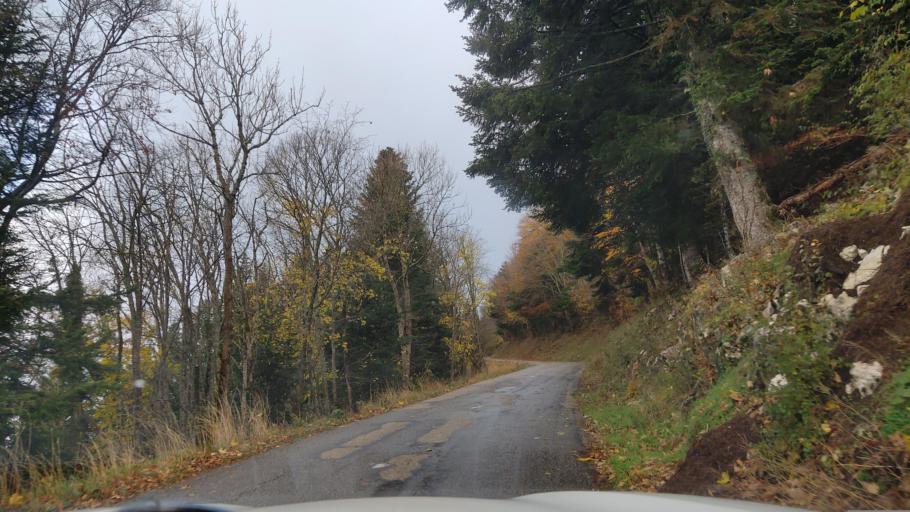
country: FR
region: Rhone-Alpes
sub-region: Departement de la Savoie
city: Le Bourget-du-Lac
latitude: 45.6488
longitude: 5.8089
